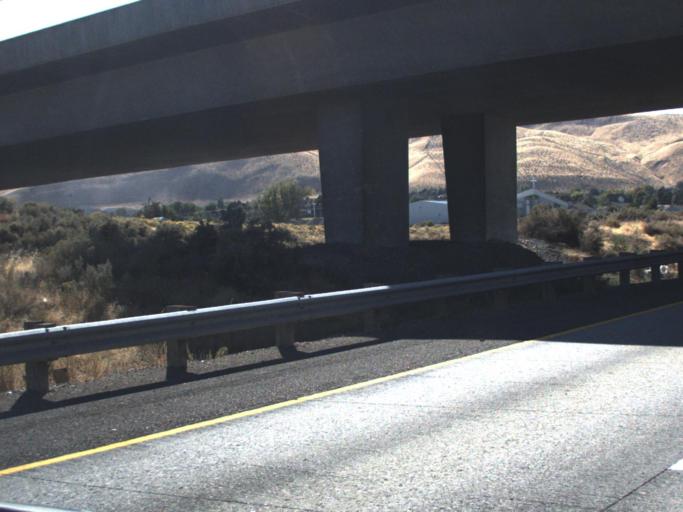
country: US
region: Washington
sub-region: Benton County
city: Richland
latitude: 46.2548
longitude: -119.3036
